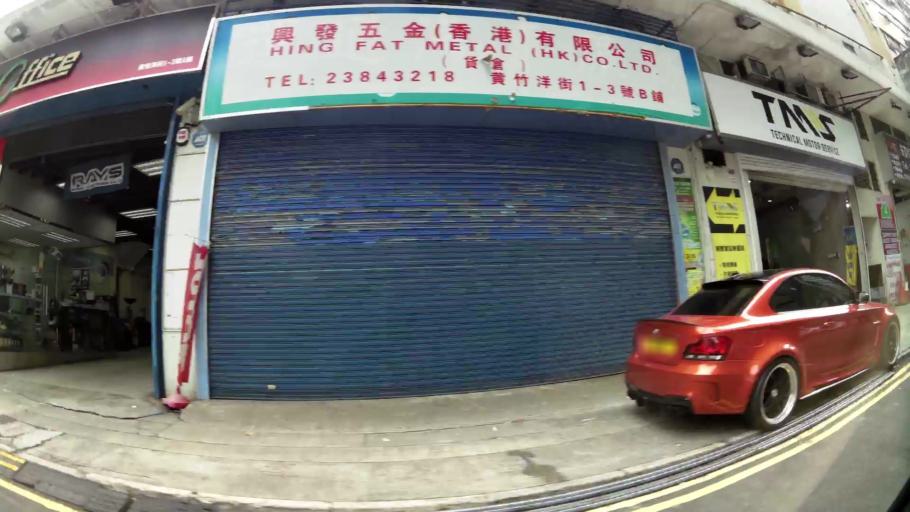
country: HK
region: Sha Tin
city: Sha Tin
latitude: 22.3970
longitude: 114.1910
